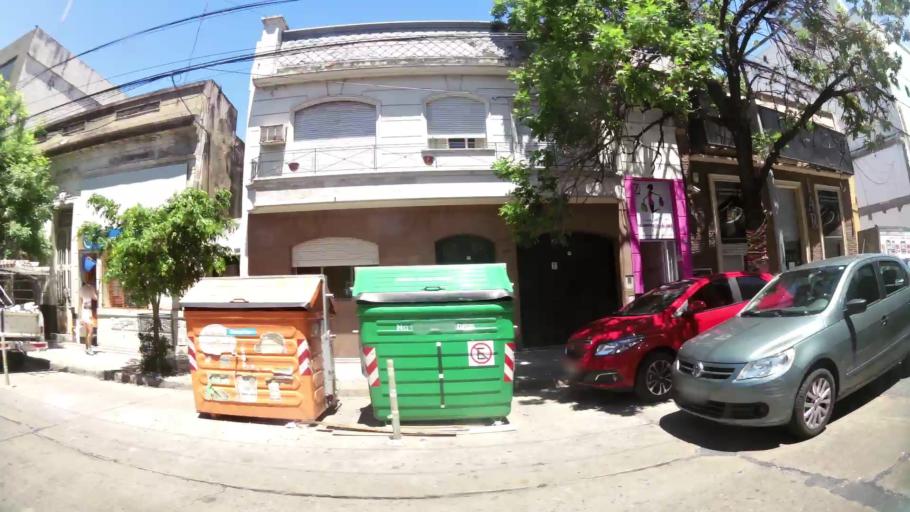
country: AR
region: Santa Fe
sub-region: Departamento de Rosario
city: Rosario
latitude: -32.9476
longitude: -60.6622
